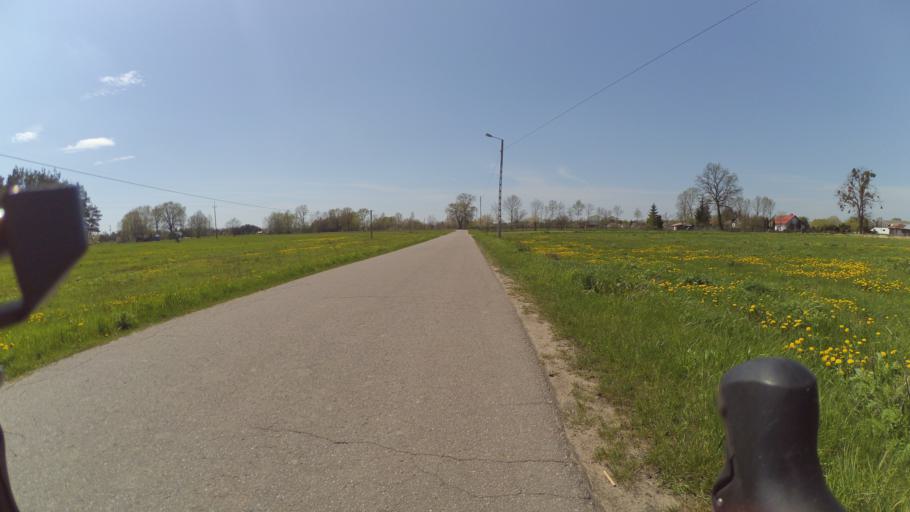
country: PL
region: Masovian Voivodeship
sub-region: Powiat nowodworski
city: Zakroczym
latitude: 52.4174
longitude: 20.5429
